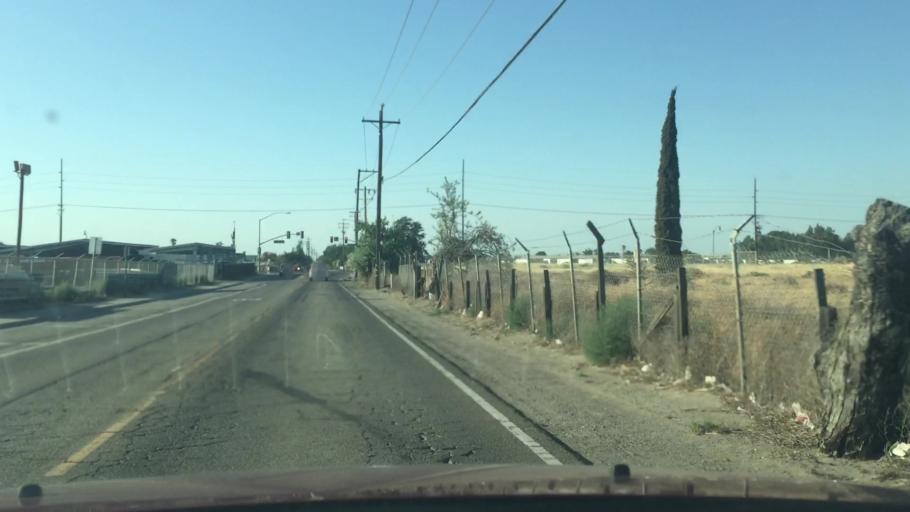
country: US
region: California
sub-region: San Joaquin County
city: Lathrop
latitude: 37.8102
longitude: -121.2713
